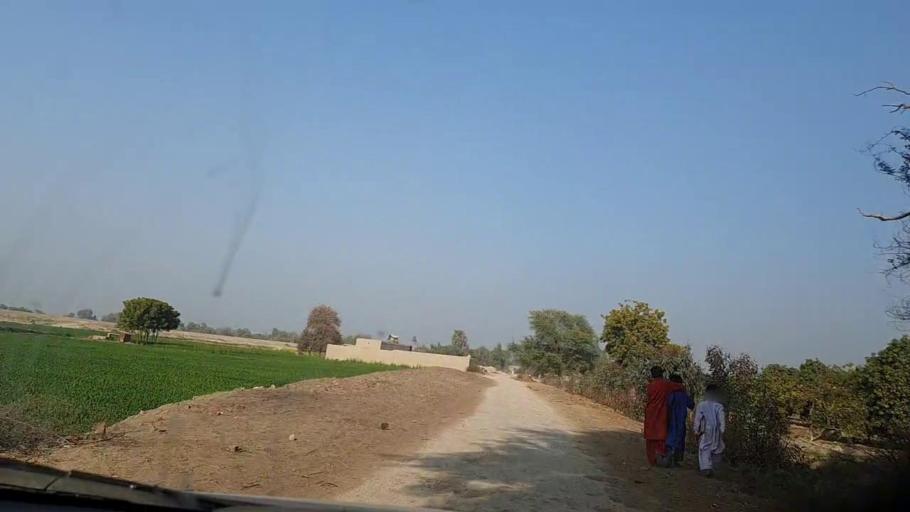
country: PK
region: Sindh
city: Moro
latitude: 26.7991
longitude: 67.9454
